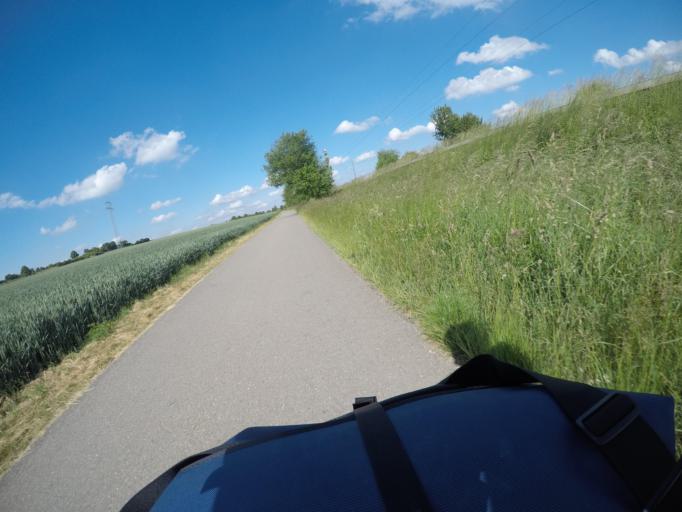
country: DE
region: Baden-Wuerttemberg
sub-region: Regierungsbezirk Stuttgart
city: Gartringen
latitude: 48.6477
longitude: 8.9173
